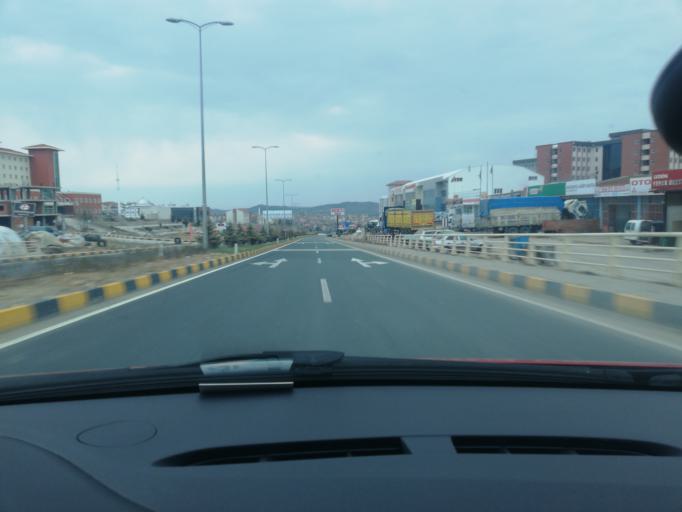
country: TR
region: Kastamonu
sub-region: Cide
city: Kastamonu
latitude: 41.4202
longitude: 33.7812
